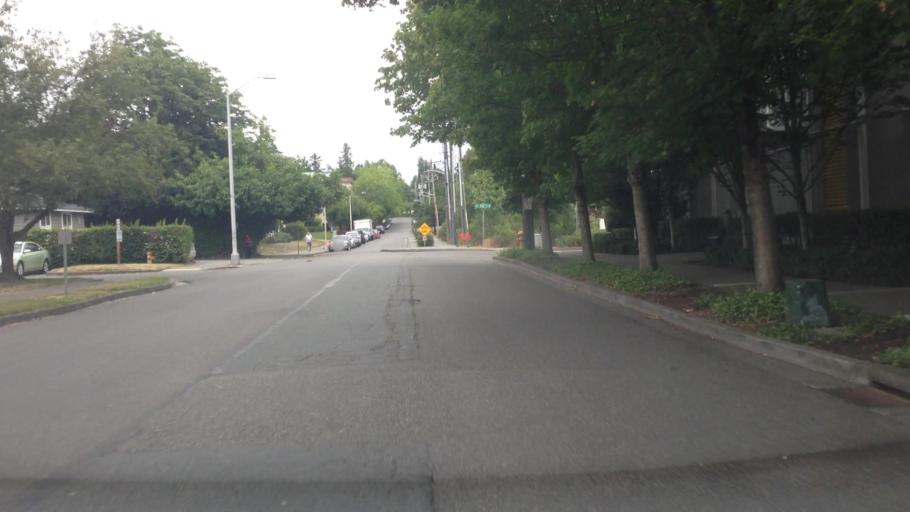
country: US
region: Washington
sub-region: King County
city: Shoreline
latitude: 47.7091
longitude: -122.3259
